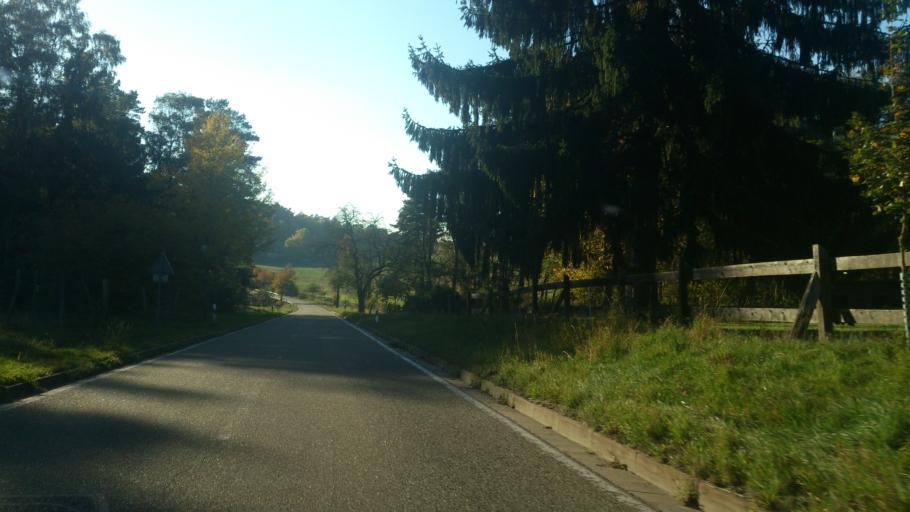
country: DE
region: Rheinland-Pfalz
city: Leimen
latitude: 49.2802
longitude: 7.7857
